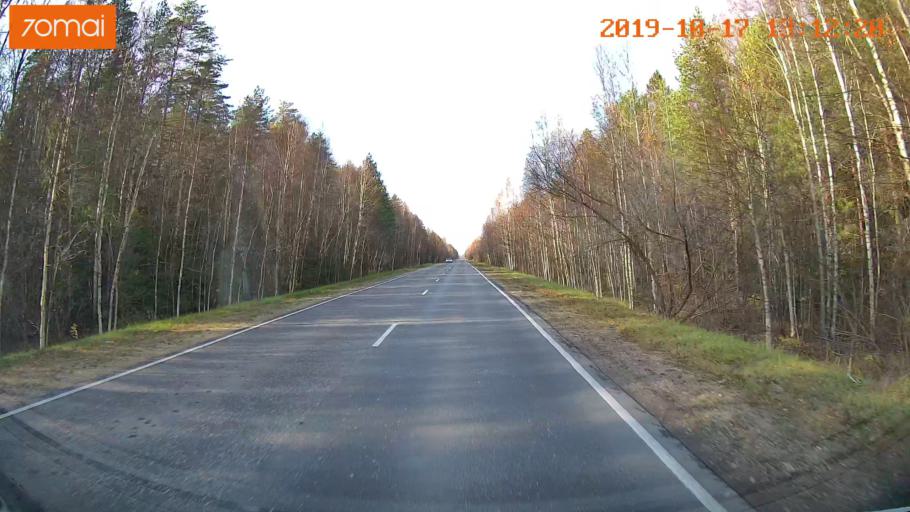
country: RU
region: Rjazan
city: Gus'-Zheleznyy
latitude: 55.0354
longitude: 41.2153
